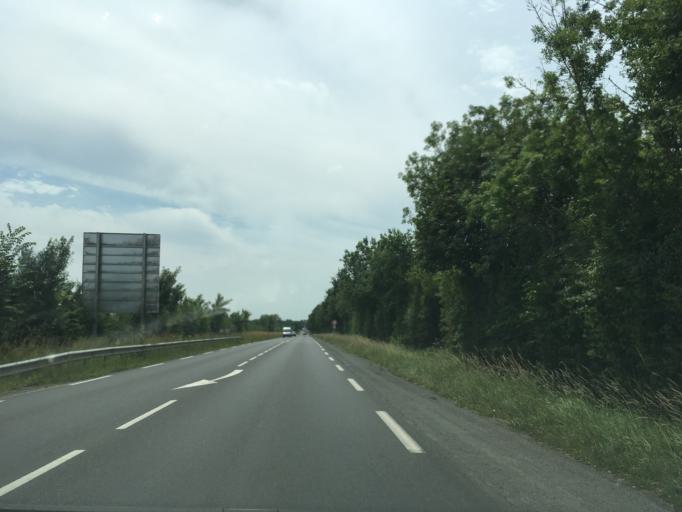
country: FR
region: Poitou-Charentes
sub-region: Departement des Deux-Sevres
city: Niort
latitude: 46.2910
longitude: -0.4659
